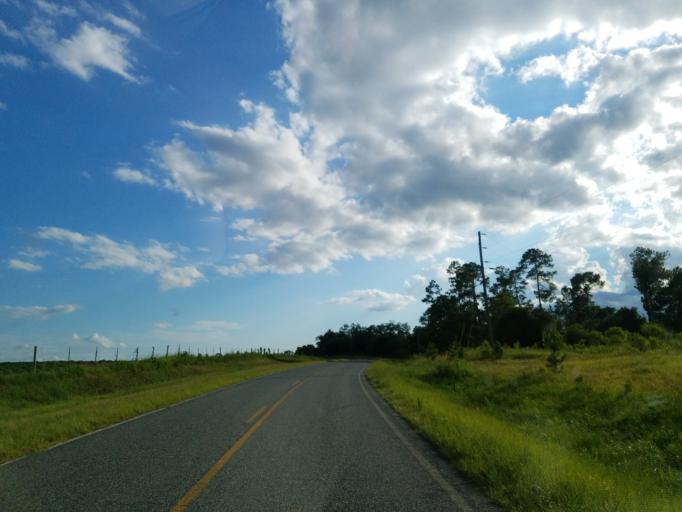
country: US
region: Georgia
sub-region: Turner County
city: Ashburn
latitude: 31.6215
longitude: -83.5895
